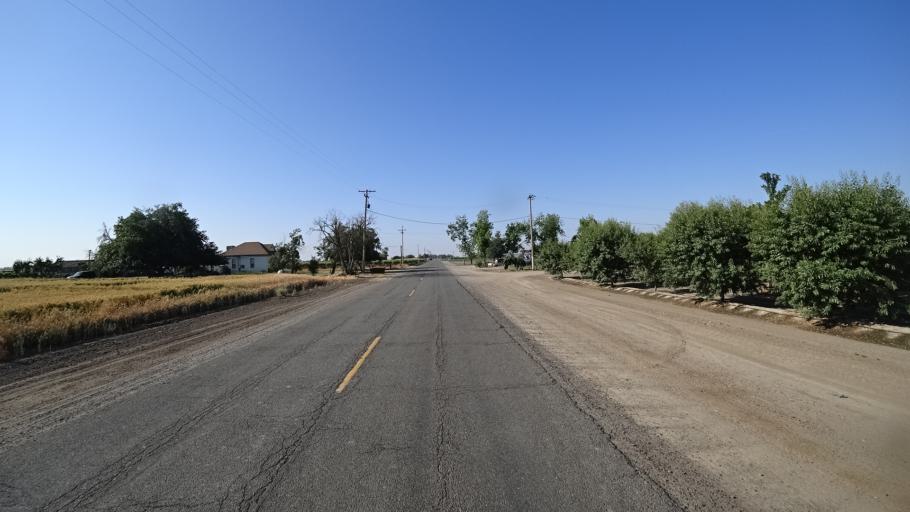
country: US
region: California
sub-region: Fresno County
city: Riverdale
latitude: 36.3703
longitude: -119.8693
